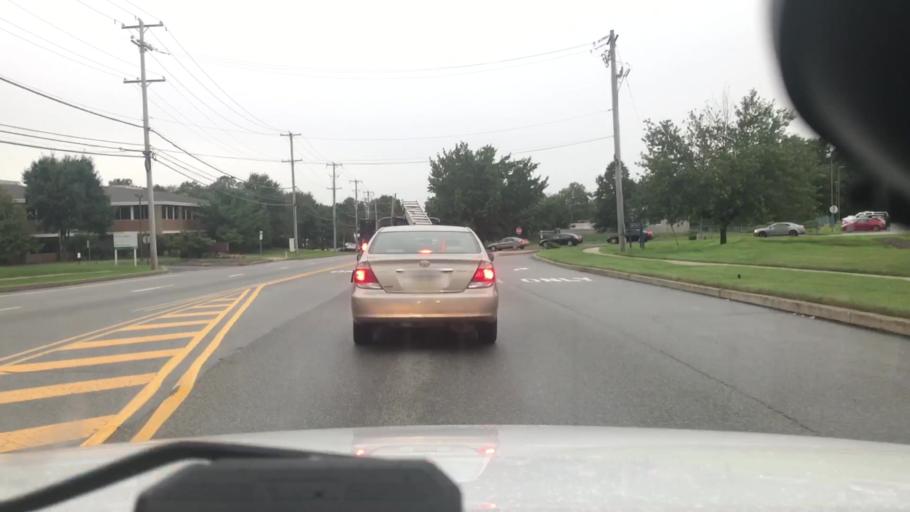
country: US
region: Pennsylvania
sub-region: Montgomery County
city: North Wales
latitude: 40.2274
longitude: -75.2598
